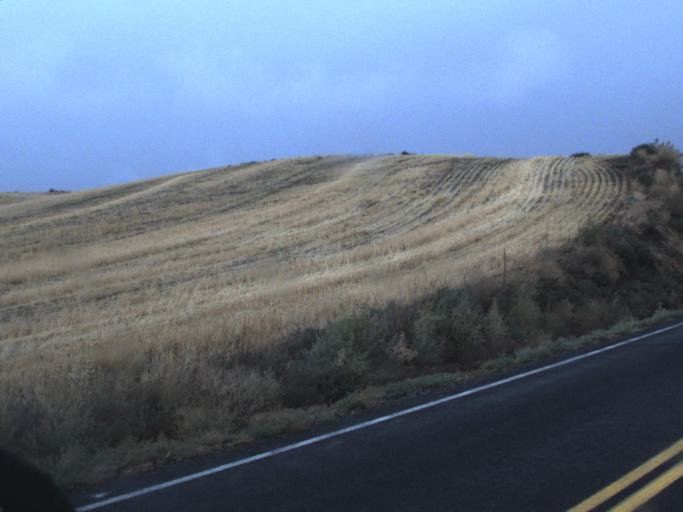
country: US
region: Washington
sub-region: Spokane County
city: Cheney
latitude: 47.1960
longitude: -117.8786
